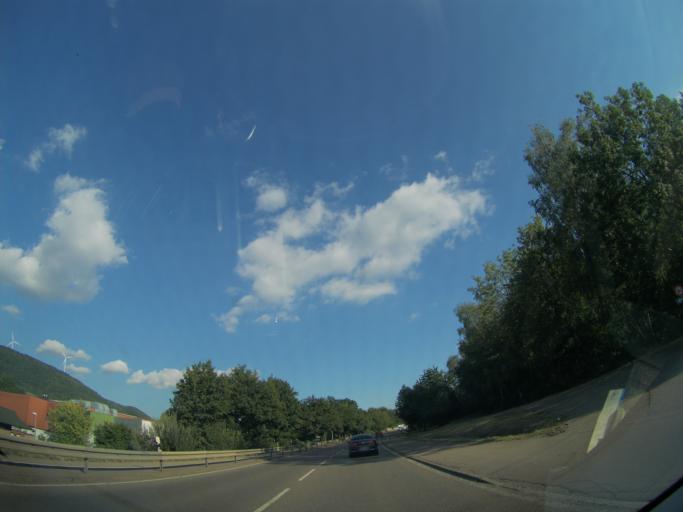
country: DE
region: Baden-Wuerttemberg
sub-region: Regierungsbezirk Stuttgart
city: Kuchen
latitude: 48.6457
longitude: 9.7886
